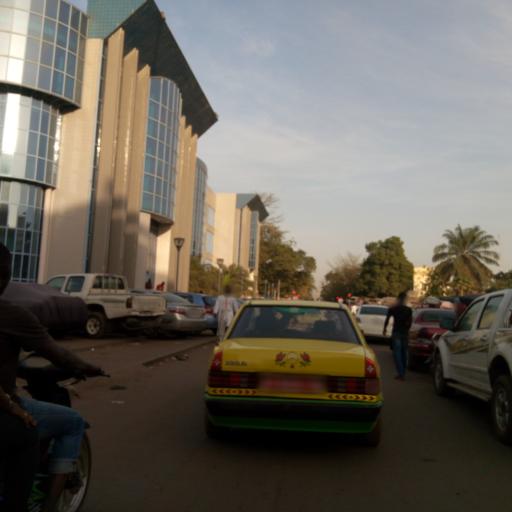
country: ML
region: Bamako
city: Bamako
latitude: 12.6456
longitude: -7.9994
